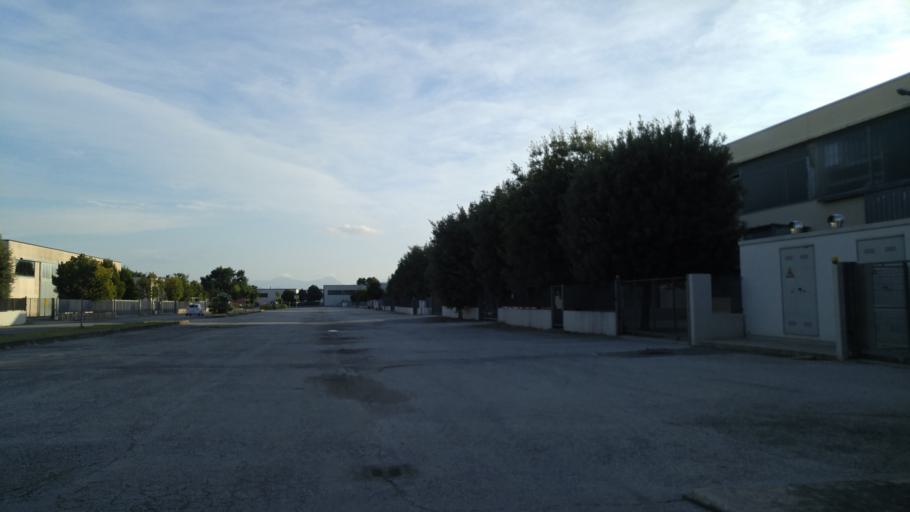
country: IT
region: The Marches
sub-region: Provincia di Pesaro e Urbino
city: Lucrezia
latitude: 43.7655
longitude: 12.9344
